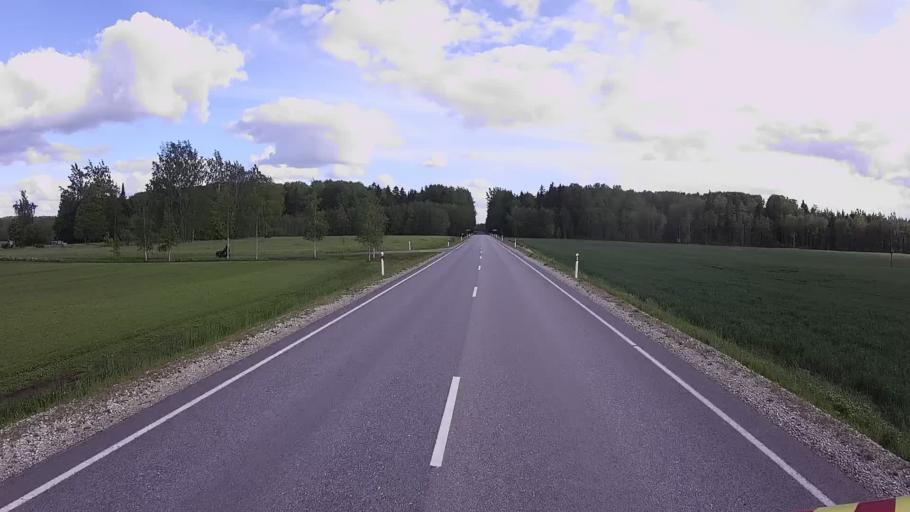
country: EE
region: Jogevamaa
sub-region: Mustvee linn
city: Mustvee
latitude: 58.8879
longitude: 26.8125
